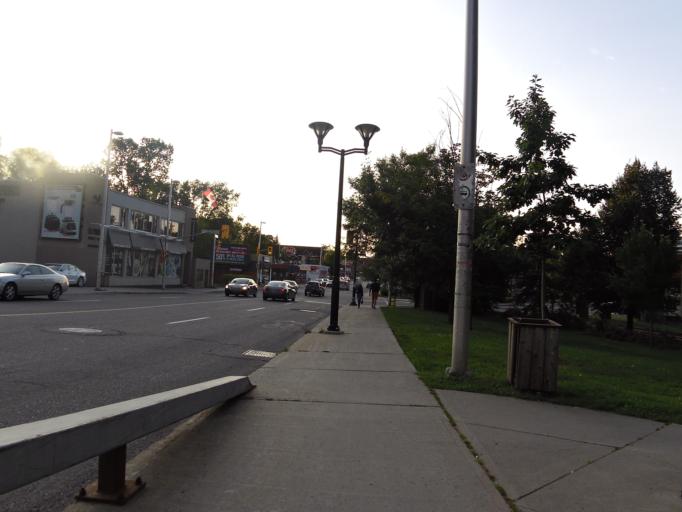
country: CA
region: Ontario
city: Ottawa
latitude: 45.3898
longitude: -75.6786
